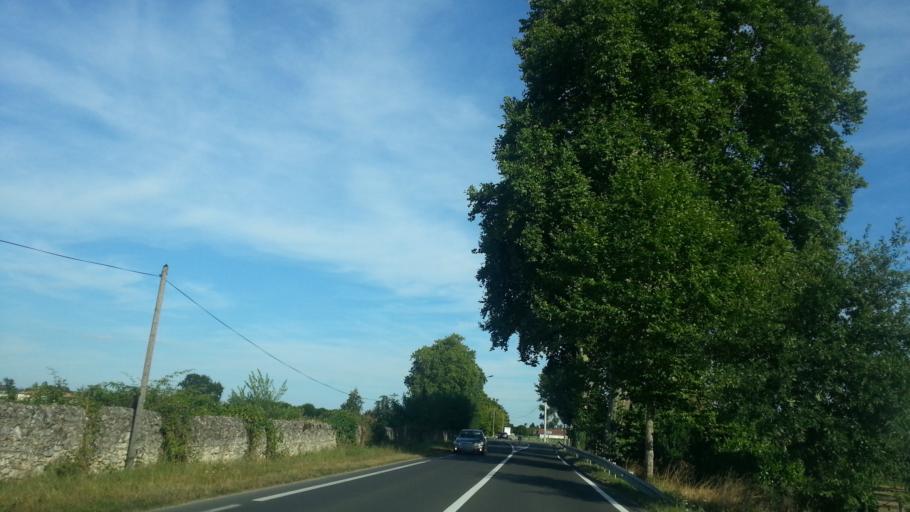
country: FR
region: Aquitaine
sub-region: Departement de la Gironde
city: Portets
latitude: 44.6922
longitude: -0.4303
